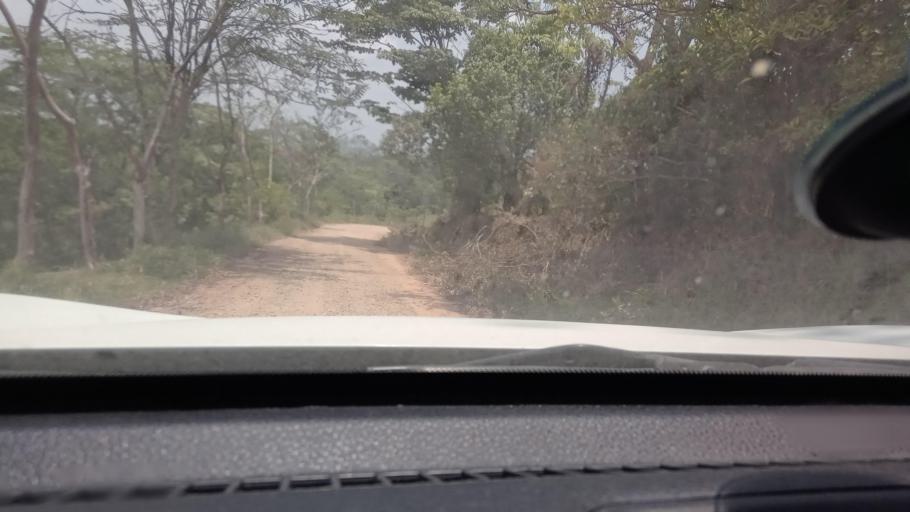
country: MX
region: Tabasco
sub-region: Huimanguillo
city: Francisco Rueda
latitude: 17.4951
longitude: -93.9115
